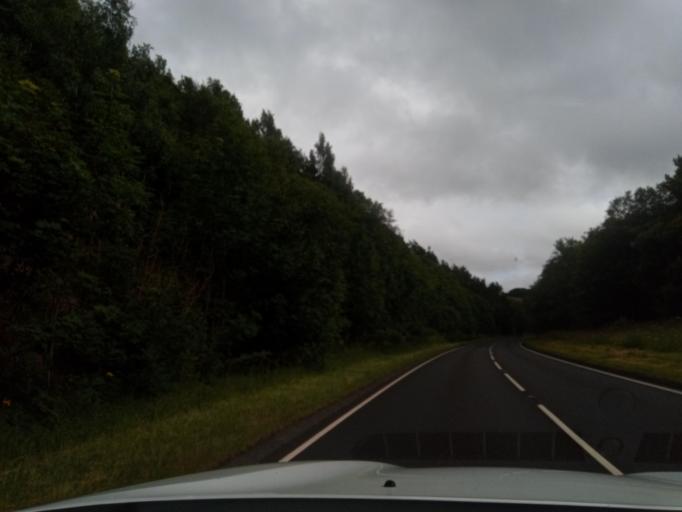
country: GB
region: Scotland
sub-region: The Scottish Borders
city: Earlston
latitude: 55.6672
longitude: -2.6944
